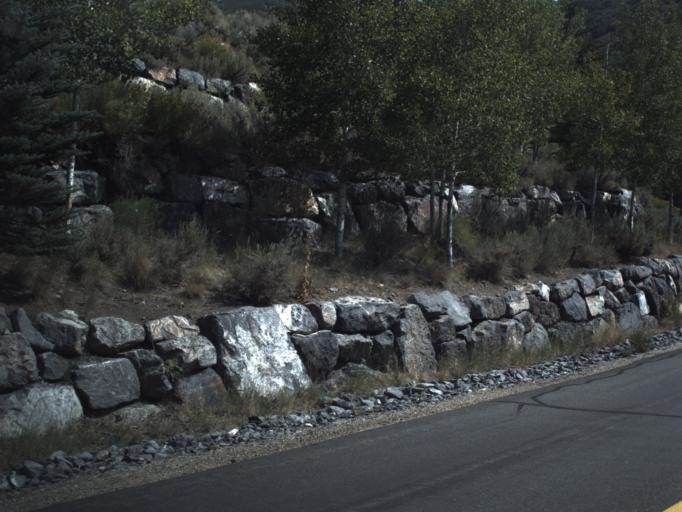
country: US
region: Utah
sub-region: Summit County
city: Snyderville
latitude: 40.7749
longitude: -111.4672
